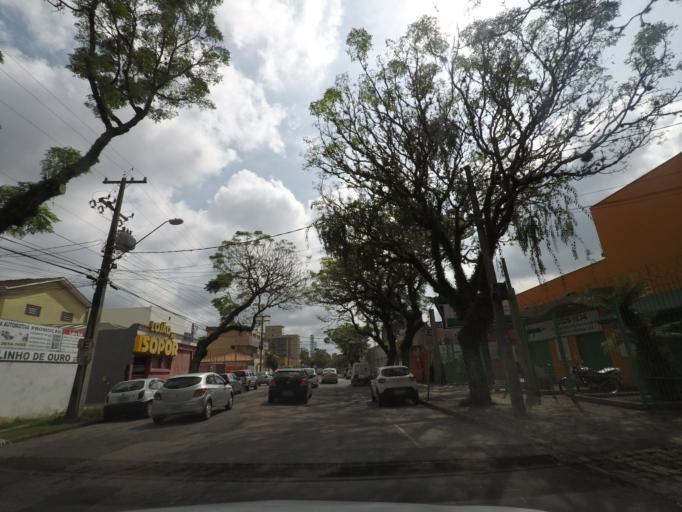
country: BR
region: Parana
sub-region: Curitiba
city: Curitiba
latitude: -25.4462
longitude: -49.2567
